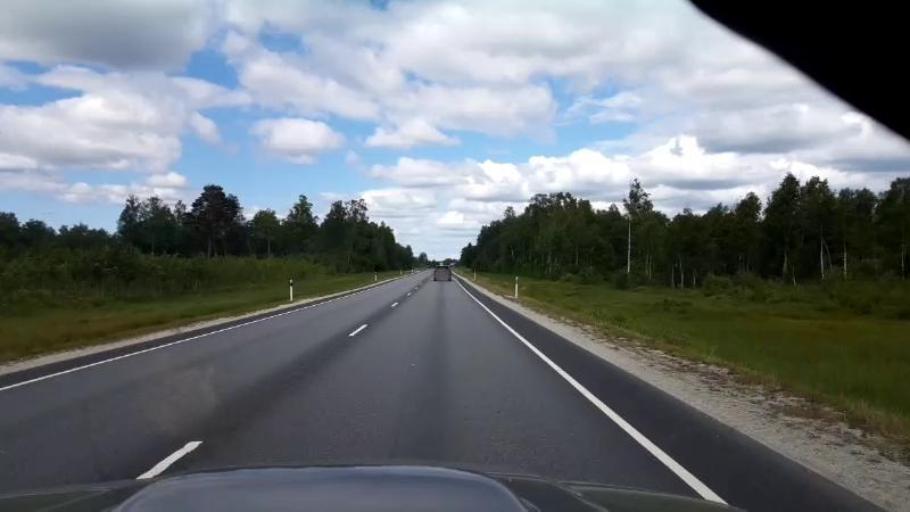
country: EE
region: Harju
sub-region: Nissi vald
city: Riisipere
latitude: 59.0688
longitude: 24.4513
